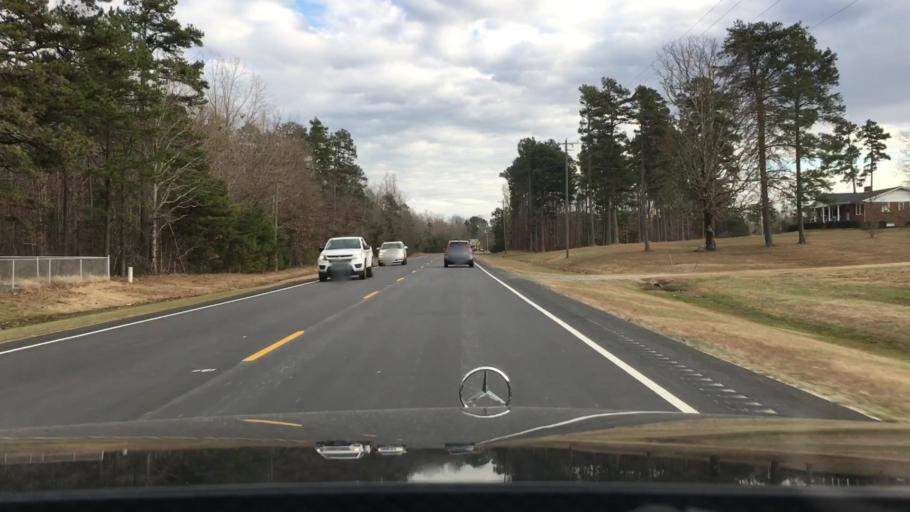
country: US
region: North Carolina
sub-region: Caswell County
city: Yanceyville
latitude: 36.2729
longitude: -79.2025
